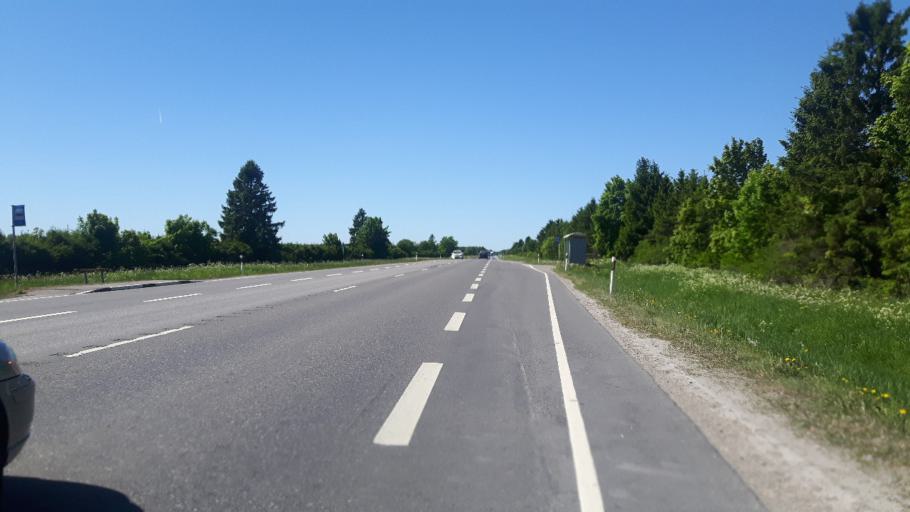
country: EE
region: Ida-Virumaa
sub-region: Sillamaee linn
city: Sillamae
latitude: 59.3919
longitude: 27.6927
